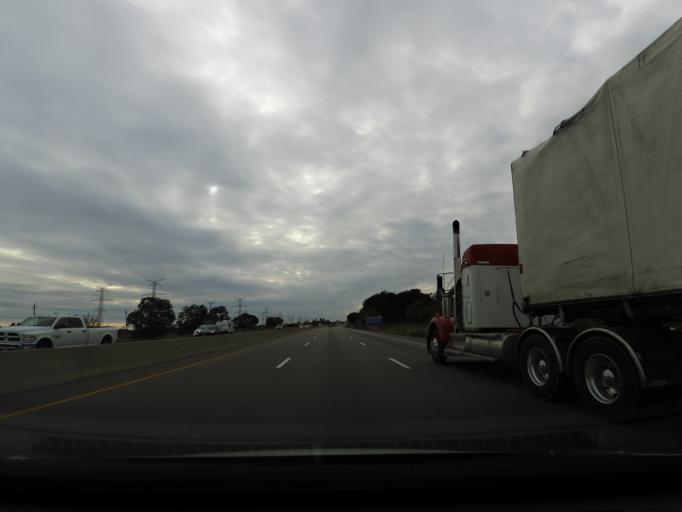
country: CA
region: Ontario
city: Oshawa
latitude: 43.9047
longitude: -78.6148
